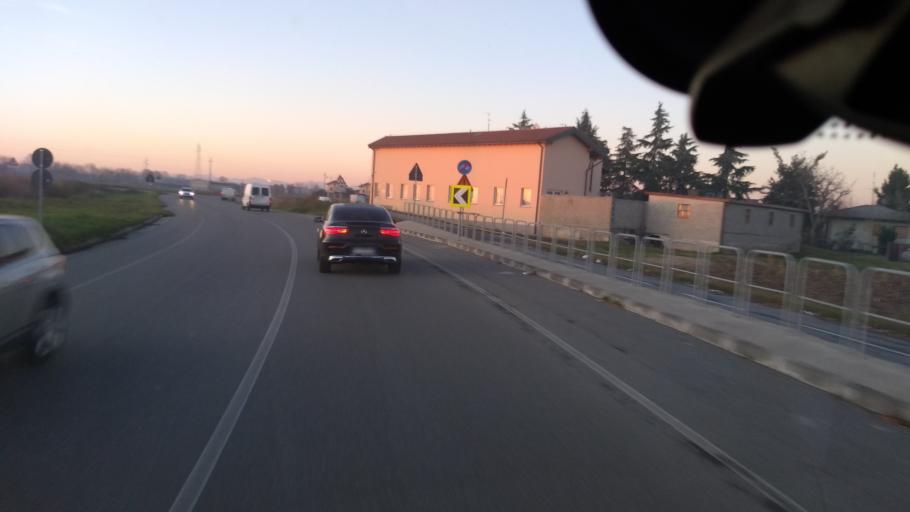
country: IT
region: Lombardy
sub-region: Provincia di Bergamo
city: Calvenzano
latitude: 45.5048
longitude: 9.5966
